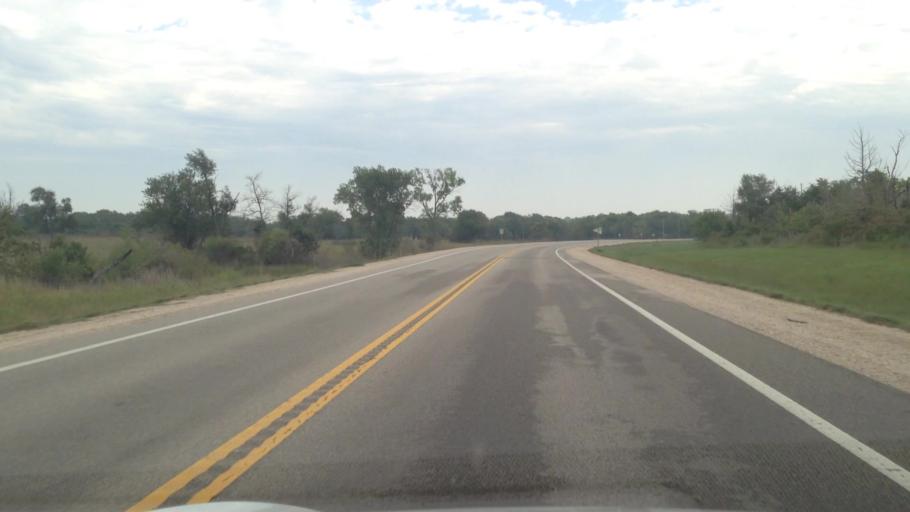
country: US
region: Kansas
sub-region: Allen County
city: Iola
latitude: 37.9082
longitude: -95.1033
